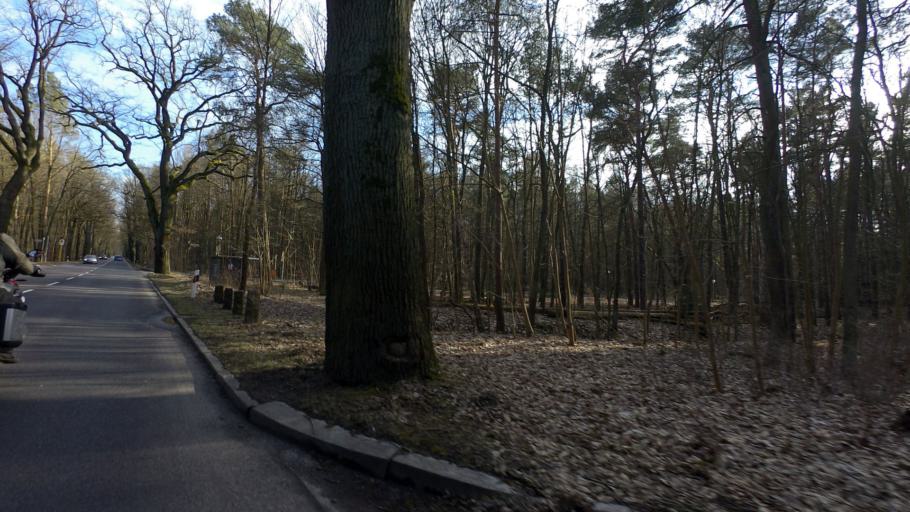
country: DE
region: Berlin
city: Frohnau
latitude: 52.6563
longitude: 13.2900
